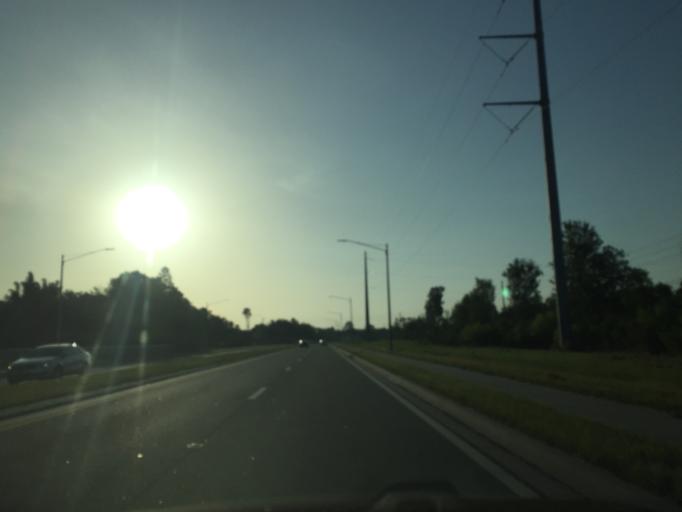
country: US
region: Florida
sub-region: Orange County
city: Alafaya
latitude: 28.5246
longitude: -81.1971
